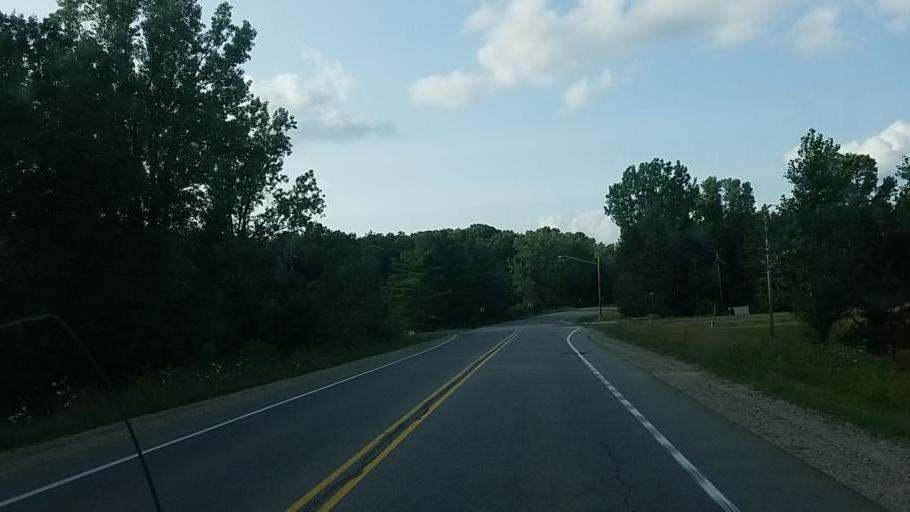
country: US
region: Michigan
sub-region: Kent County
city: Lowell
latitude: 42.8993
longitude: -85.3711
